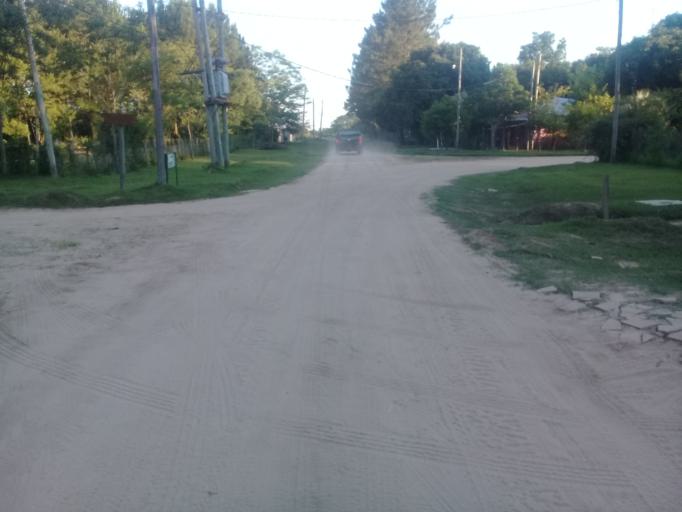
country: AR
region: Corrientes
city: San Luis del Palmar
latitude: -27.4664
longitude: -58.6646
